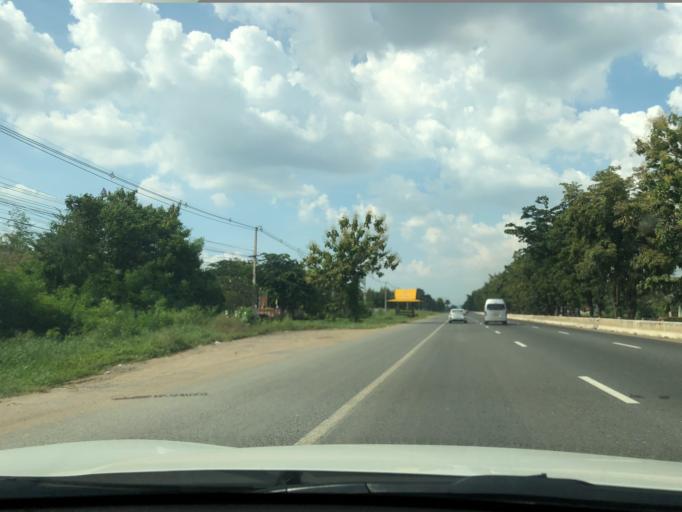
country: TH
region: Nakhon Sawan
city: Krok Phra
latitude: 15.5788
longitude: 100.1246
